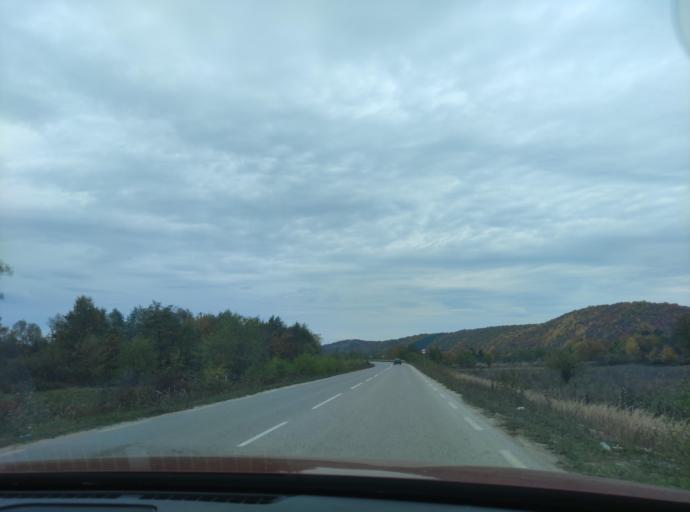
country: BG
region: Montana
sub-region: Obshtina Berkovitsa
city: Berkovitsa
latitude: 43.2470
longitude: 23.1663
